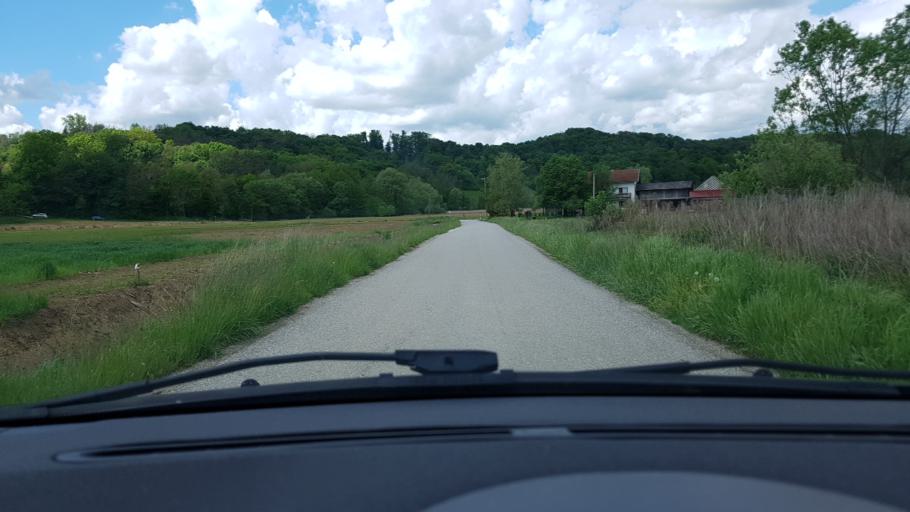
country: HR
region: Krapinsko-Zagorska
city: Pregrada
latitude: 46.1421
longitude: 15.8091
